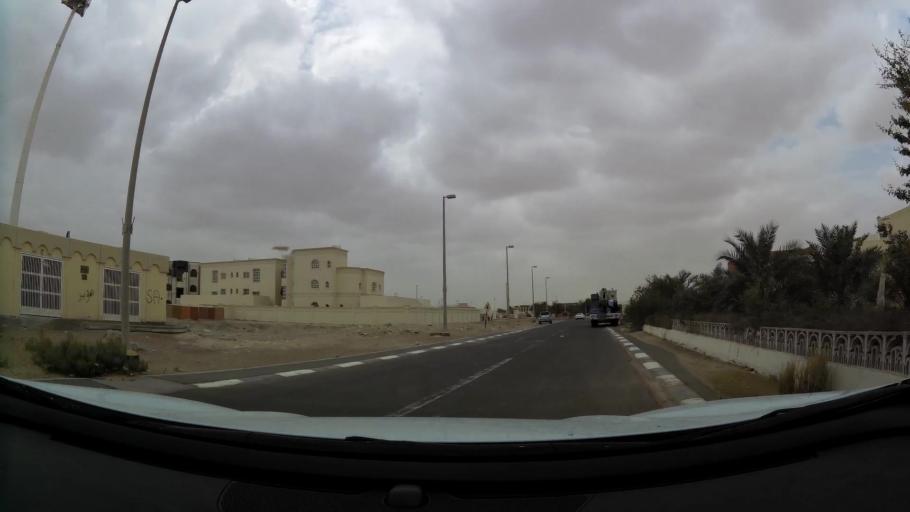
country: AE
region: Abu Dhabi
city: Abu Dhabi
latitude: 24.3329
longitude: 54.6395
